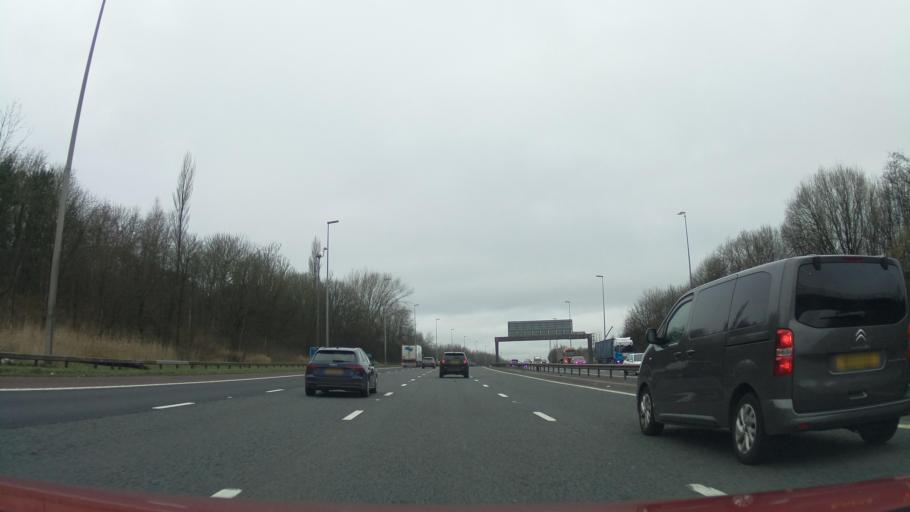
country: GB
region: England
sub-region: Lancashire
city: Goosnargh
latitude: 53.7767
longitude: -2.6450
